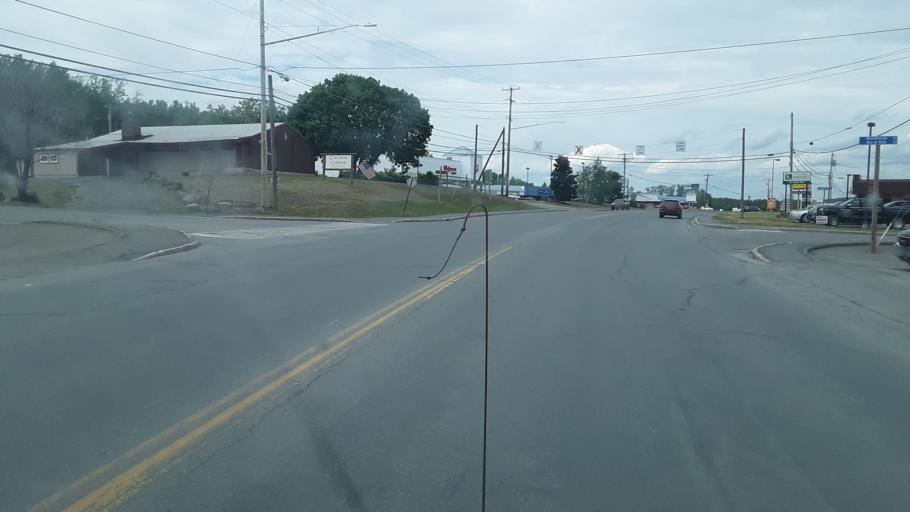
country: US
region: Maine
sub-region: Aroostook County
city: Caribou
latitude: 46.8673
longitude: -68.0048
